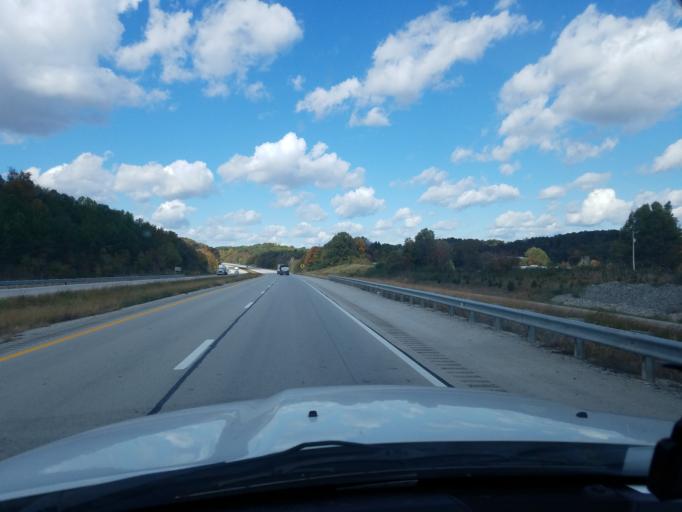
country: US
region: Kentucky
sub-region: Butler County
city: Morgantown
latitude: 37.2158
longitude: -86.7117
